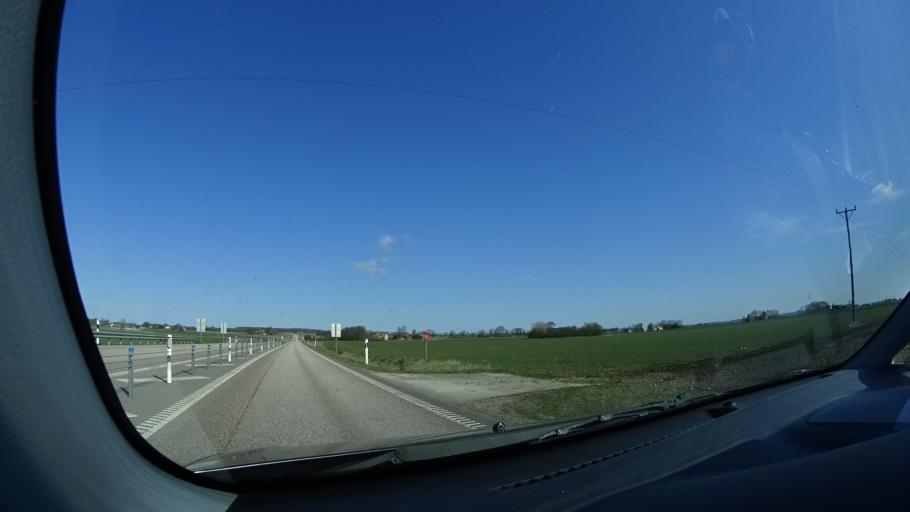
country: SE
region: Skane
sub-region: Astorps Kommun
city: Astorp
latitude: 56.1565
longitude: 12.9197
